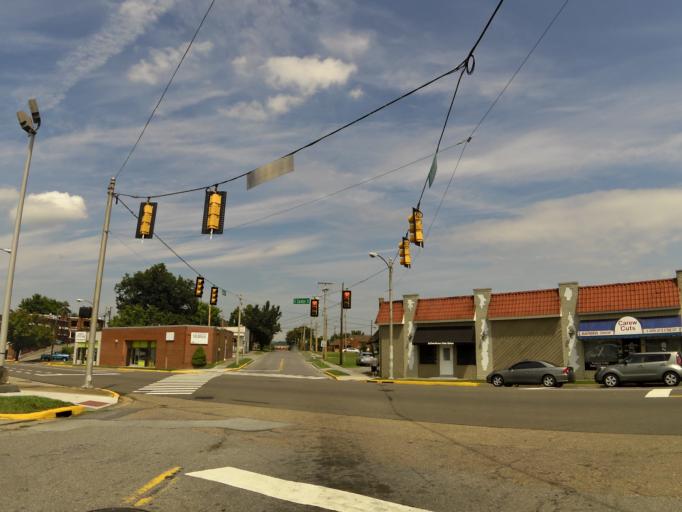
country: US
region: Tennessee
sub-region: Sullivan County
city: Kingsport
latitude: 36.5438
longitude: -82.5529
